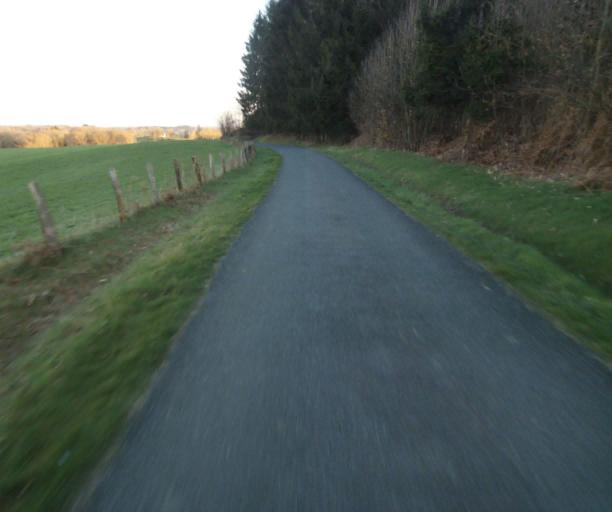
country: FR
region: Limousin
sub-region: Departement de la Correze
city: Uzerche
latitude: 45.3779
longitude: 1.6047
